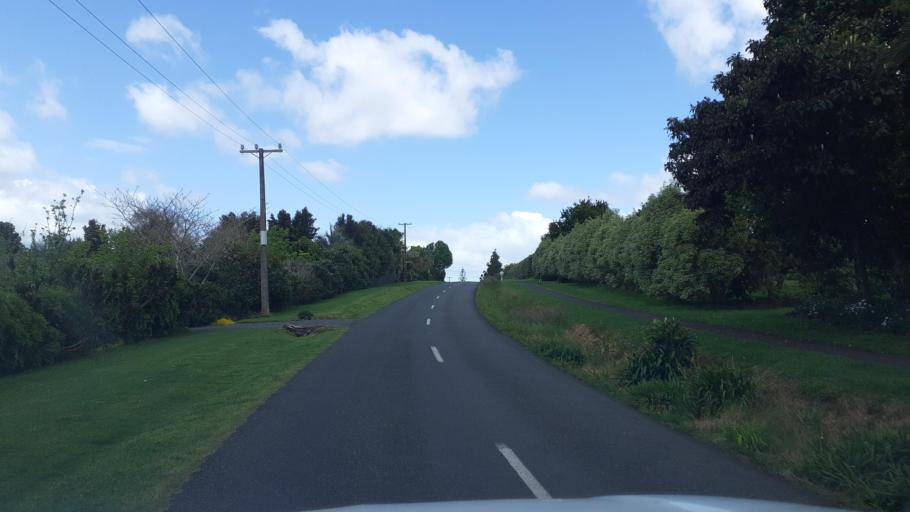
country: NZ
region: Northland
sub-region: Far North District
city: Kerikeri
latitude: -35.2397
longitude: 173.9593
